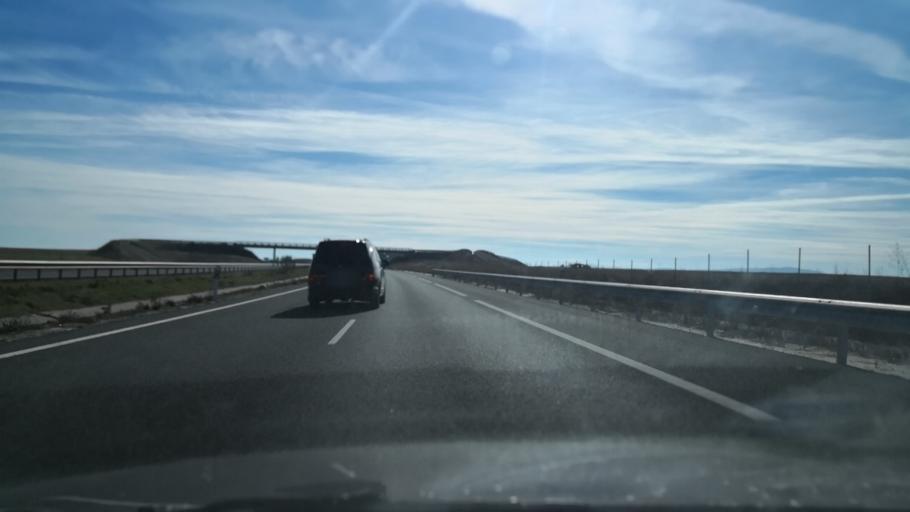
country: ES
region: Castille and Leon
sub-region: Provincia de Avila
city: Crespos
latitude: 40.8565
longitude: -4.9832
